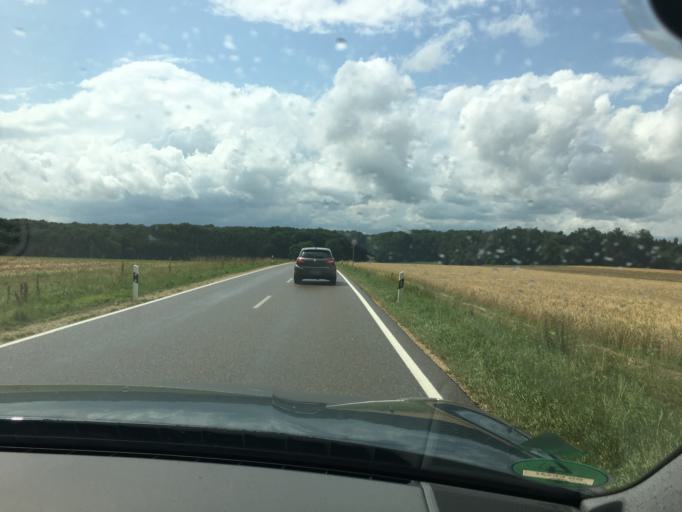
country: DE
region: Baden-Wuerttemberg
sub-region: Tuebingen Region
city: Nellingen
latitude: 48.5131
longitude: 9.7938
